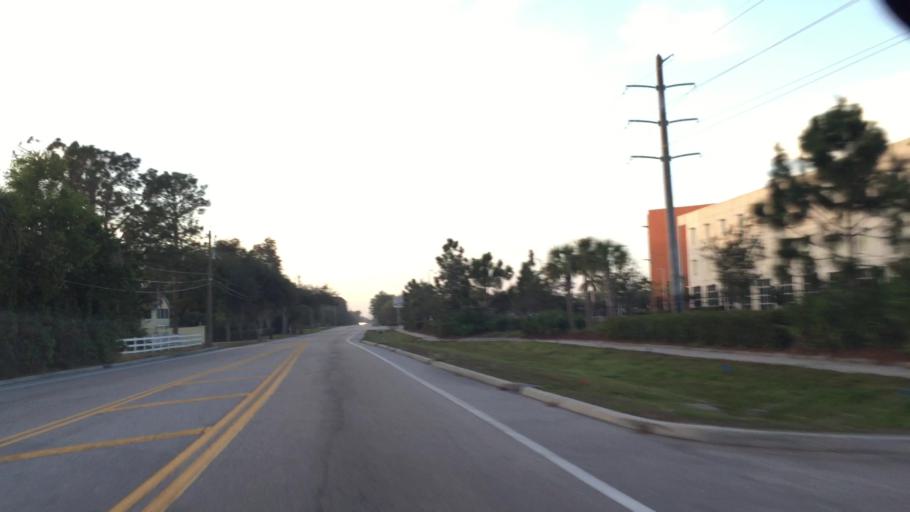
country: US
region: Florida
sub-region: Lee County
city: Pine Manor
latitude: 26.5820
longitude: -81.8473
